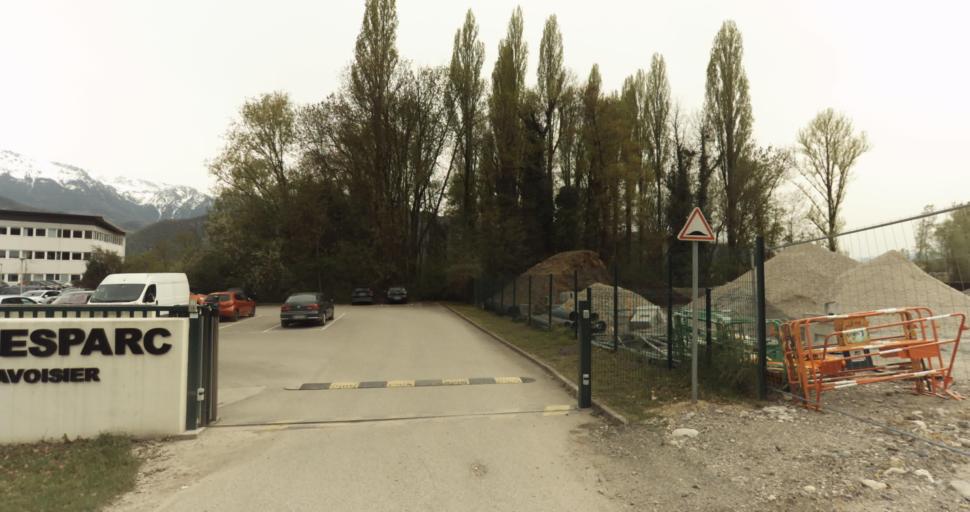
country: FR
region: Rhone-Alpes
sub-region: Departement de l'Isere
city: Montbonnot-Saint-Martin
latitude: 45.2168
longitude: 5.8131
